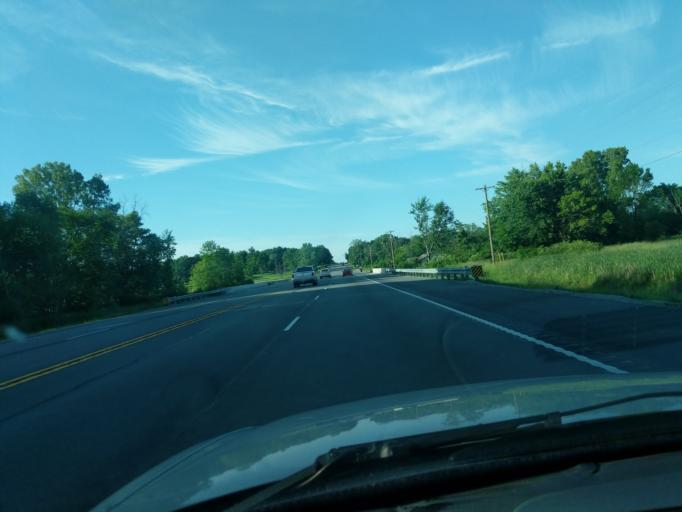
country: US
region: Indiana
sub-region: Madison County
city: Pendleton
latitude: 40.0241
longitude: -85.7301
